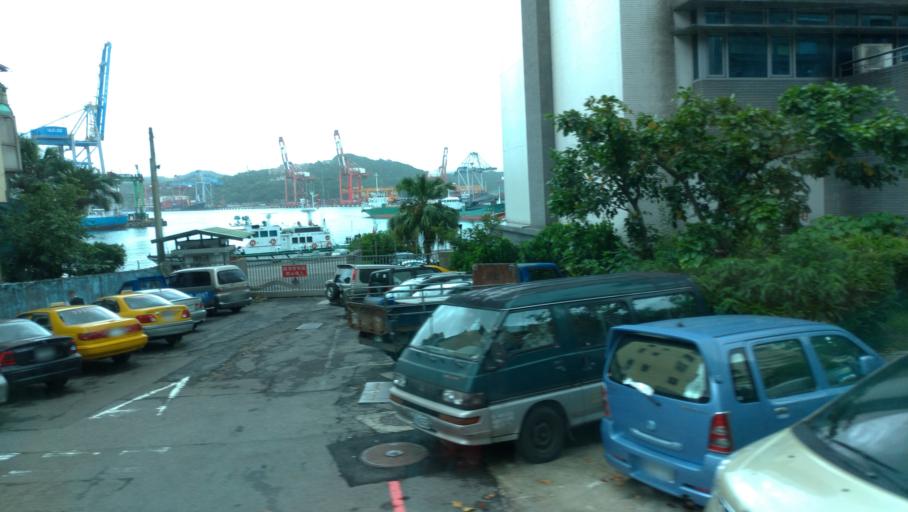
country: TW
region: Taiwan
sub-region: Keelung
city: Keelung
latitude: 25.1439
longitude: 121.7615
